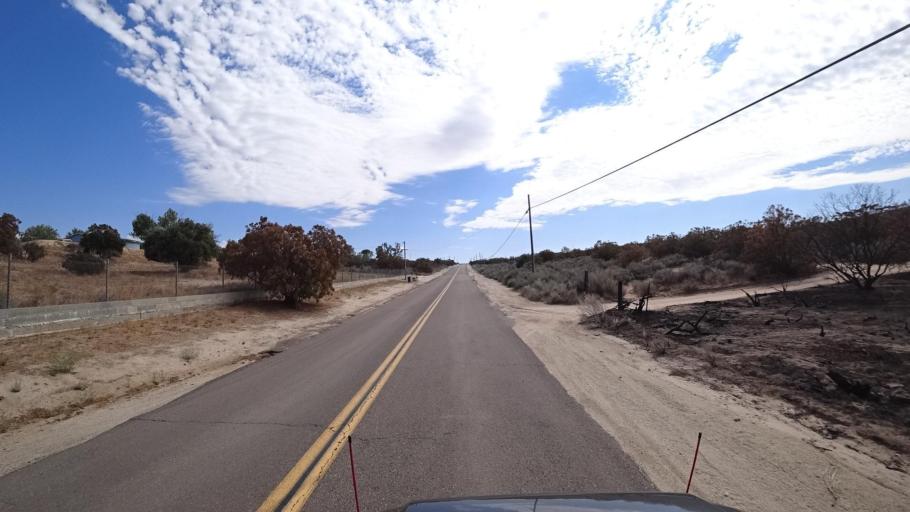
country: MX
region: Baja California
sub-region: Tecate
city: Cereso del Hongo
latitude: 32.6621
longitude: -116.2903
